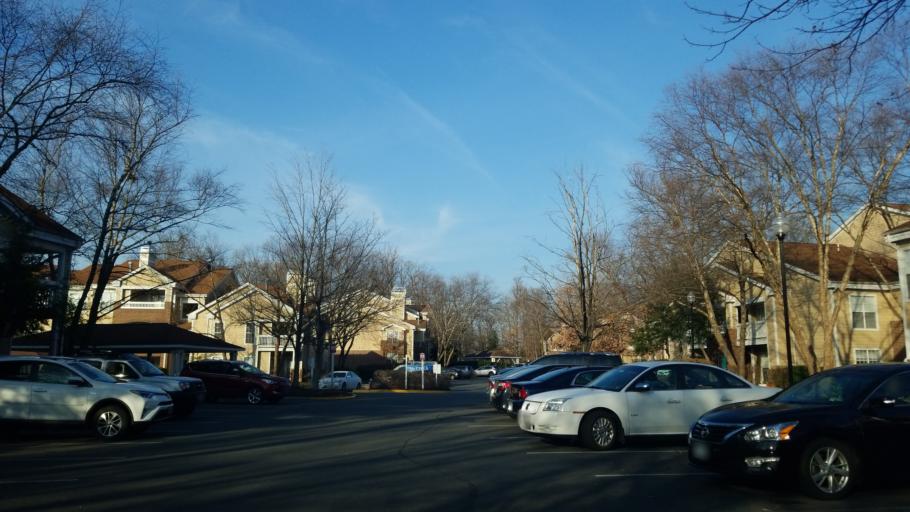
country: US
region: Virginia
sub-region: Fairfax County
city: Greenbriar
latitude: 38.8581
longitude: -77.3984
